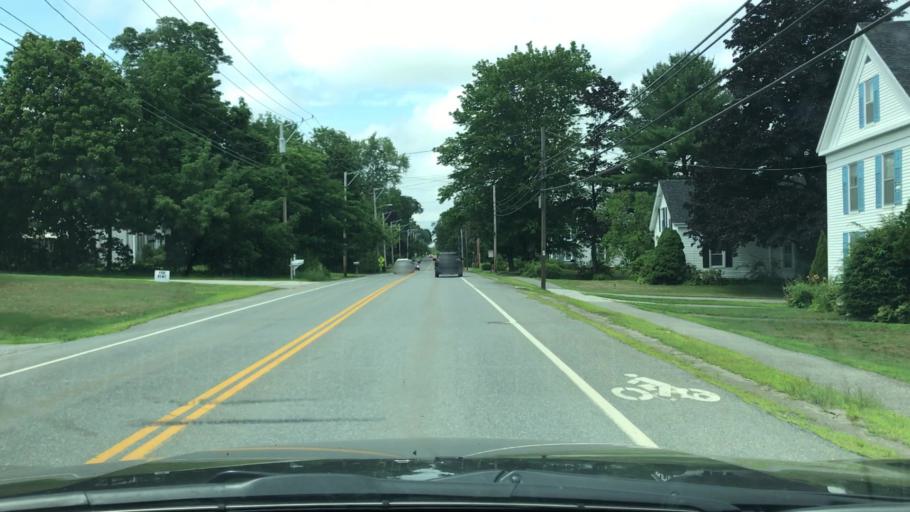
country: US
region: Maine
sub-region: Waldo County
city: Belfast
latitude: 44.4153
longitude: -68.9965
